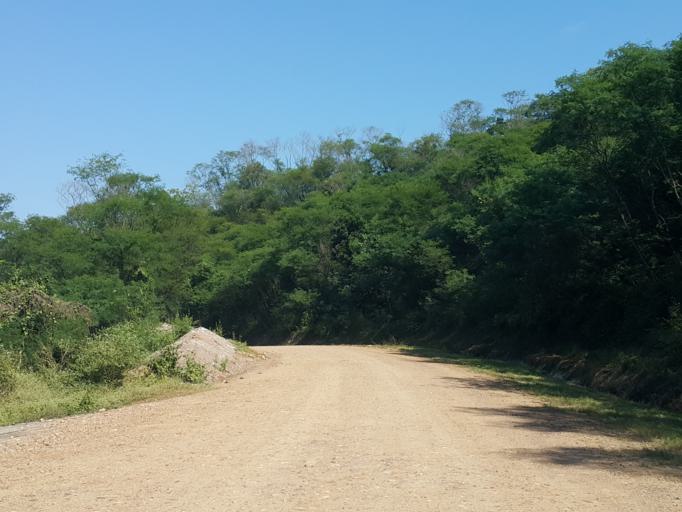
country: TH
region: Lampang
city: Mae Mo
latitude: 18.3270
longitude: 99.7397
